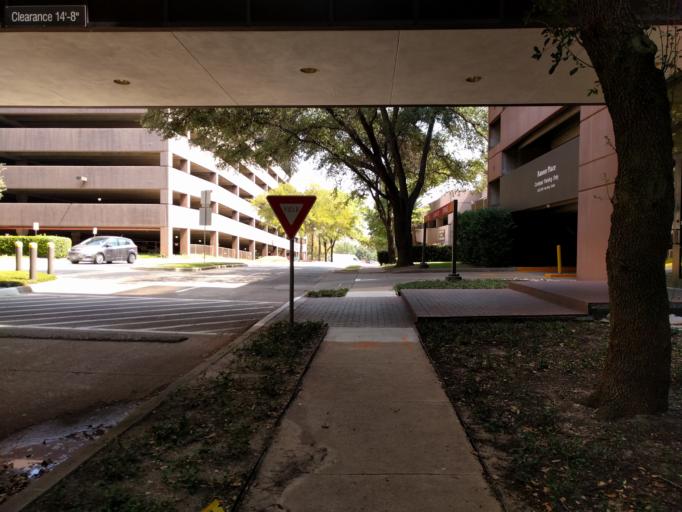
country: US
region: Texas
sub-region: Dallas County
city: Richardson
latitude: 32.9212
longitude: -96.7682
